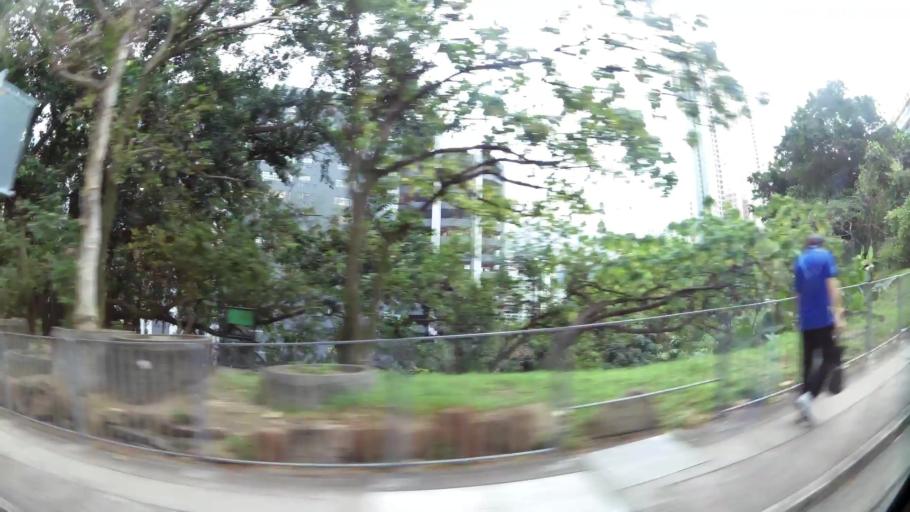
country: HK
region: Tsuen Wan
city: Tsuen Wan
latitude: 22.3625
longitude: 114.1223
